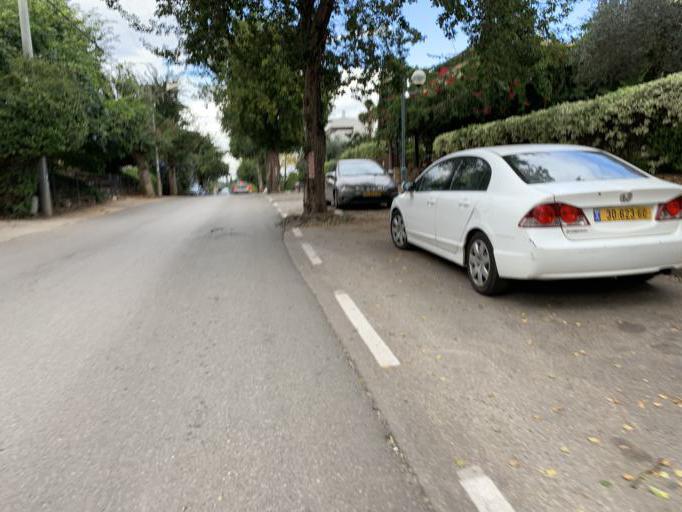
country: IL
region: Central District
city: Hod HaSharon
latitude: 32.1574
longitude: 34.8870
